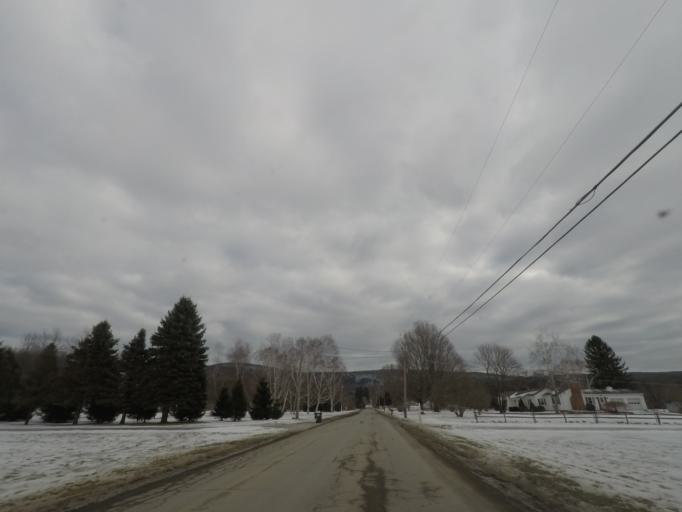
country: US
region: New York
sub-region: Rensselaer County
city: Poestenkill
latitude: 42.7372
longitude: -73.5682
